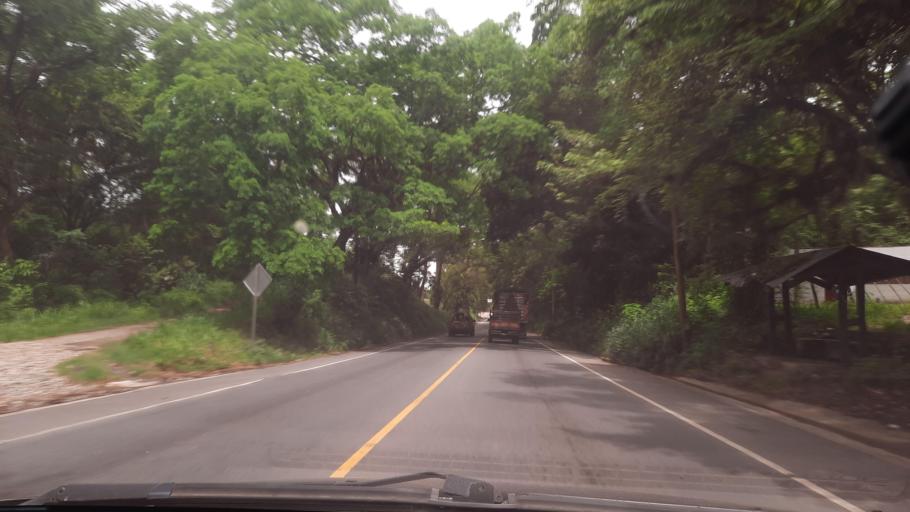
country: GT
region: Zacapa
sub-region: Municipio de Zacapa
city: Gualan
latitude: 15.2044
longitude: -89.2530
